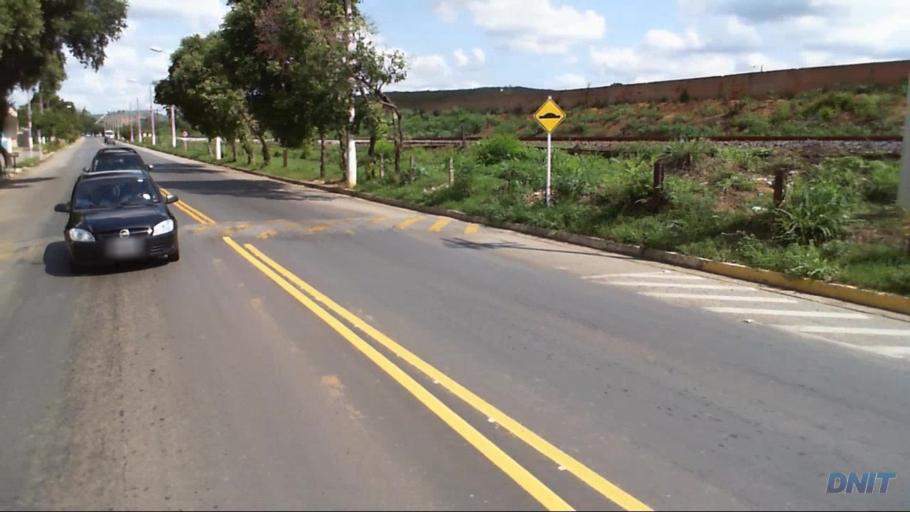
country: BR
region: Minas Gerais
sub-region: Governador Valadares
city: Governador Valadares
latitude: -18.9072
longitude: -41.9921
